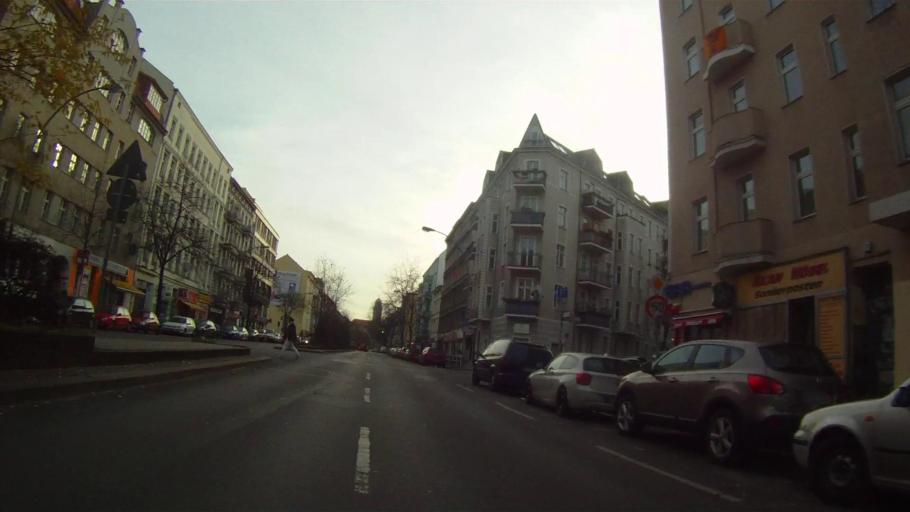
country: DE
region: Berlin
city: Berlin Treptow
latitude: 52.4851
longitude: 13.4271
